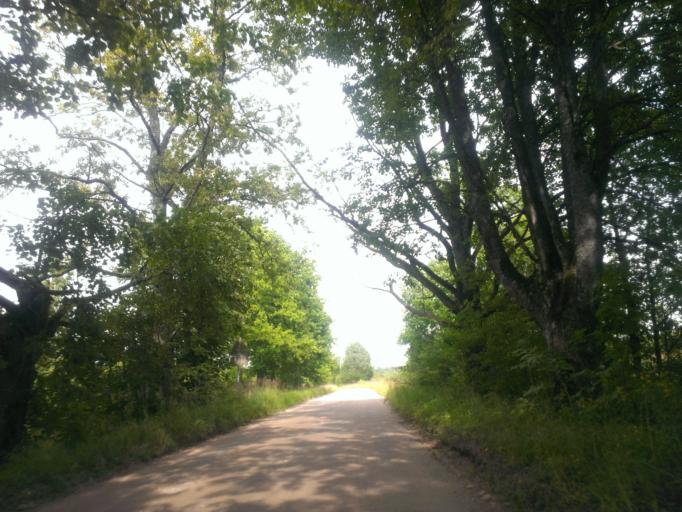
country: LV
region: Ligatne
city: Ligatne
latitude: 57.2130
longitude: 25.0197
